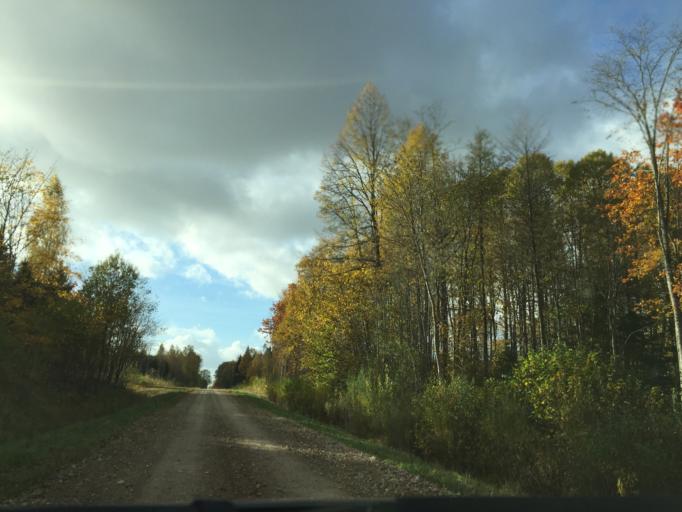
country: LV
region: Ogre
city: Jumprava
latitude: 56.7395
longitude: 24.9283
